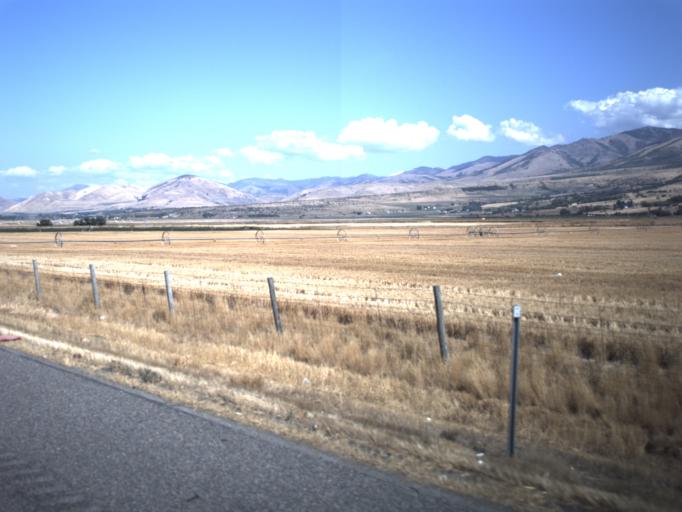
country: US
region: Utah
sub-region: Cache County
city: Lewiston
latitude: 41.9692
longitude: -111.8127
